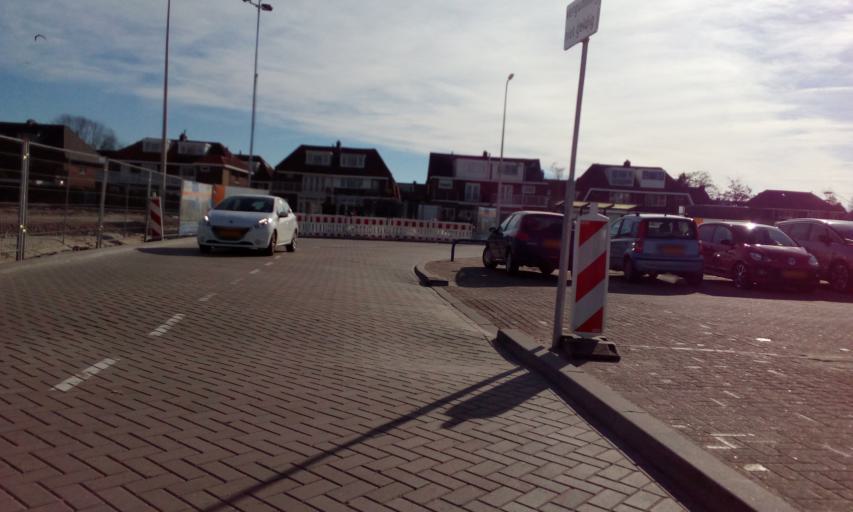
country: NL
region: South Holland
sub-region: Gemeente Alphen aan den Rijn
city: Alphen aan den Rijn
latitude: 52.1300
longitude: 4.6667
